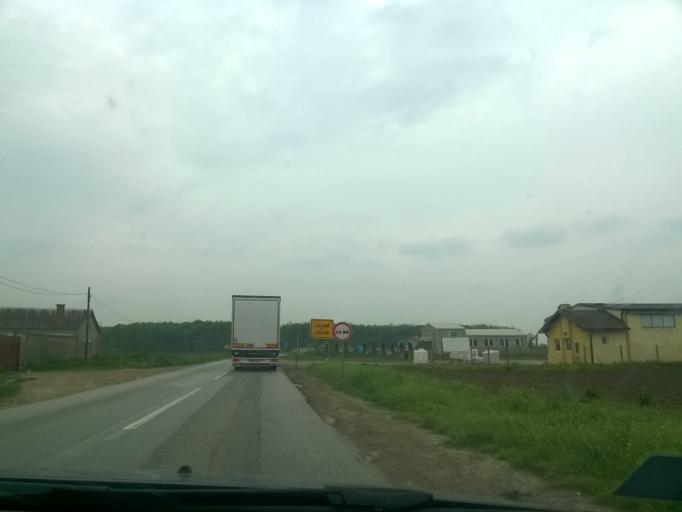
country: RS
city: Jarak
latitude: 44.9077
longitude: 19.7647
